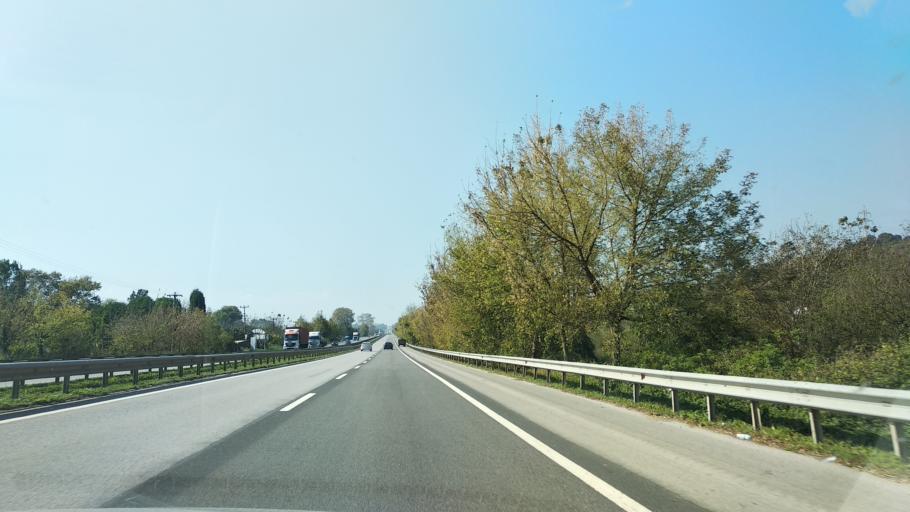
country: TR
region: Sakarya
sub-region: Merkez
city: Sapanca
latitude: 40.7329
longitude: 30.2103
